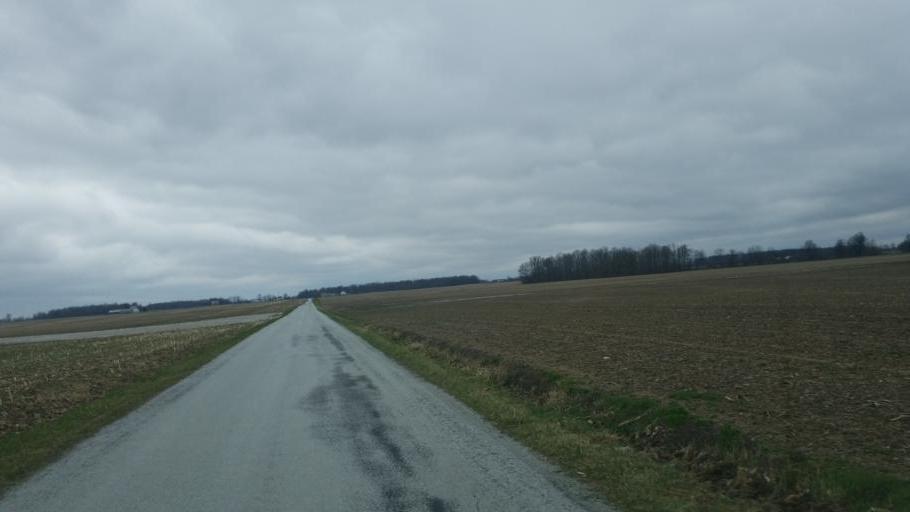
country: US
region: Ohio
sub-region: Hardin County
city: Forest
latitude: 40.7237
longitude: -83.5223
